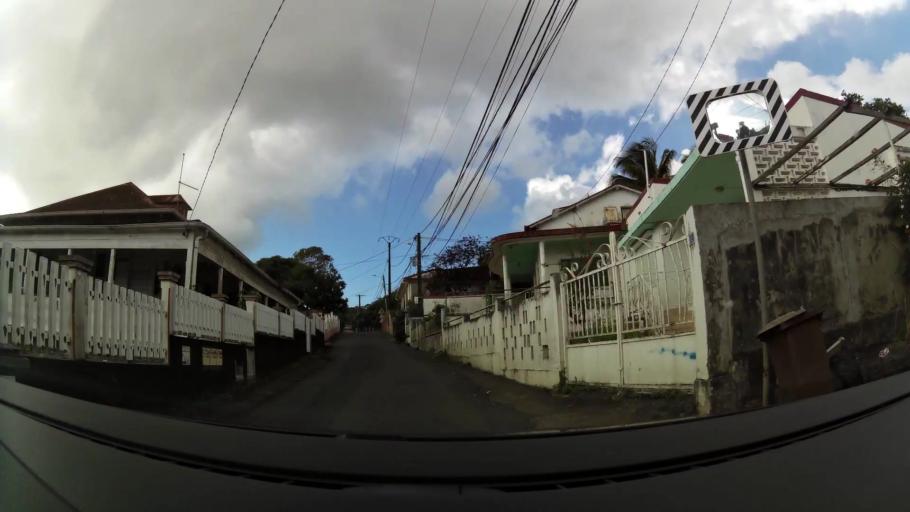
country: GP
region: Guadeloupe
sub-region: Guadeloupe
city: Trois-Rivieres
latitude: 15.9771
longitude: -61.6420
